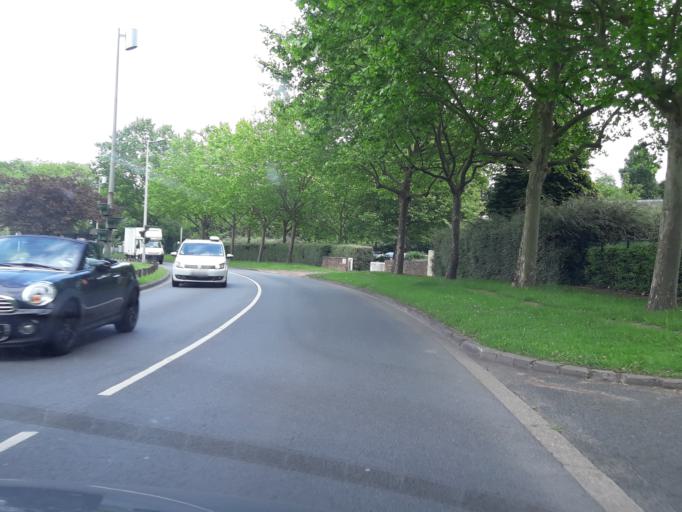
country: FR
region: Ile-de-France
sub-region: Departement de l'Essonne
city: Lisses
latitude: 48.6119
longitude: 2.4215
